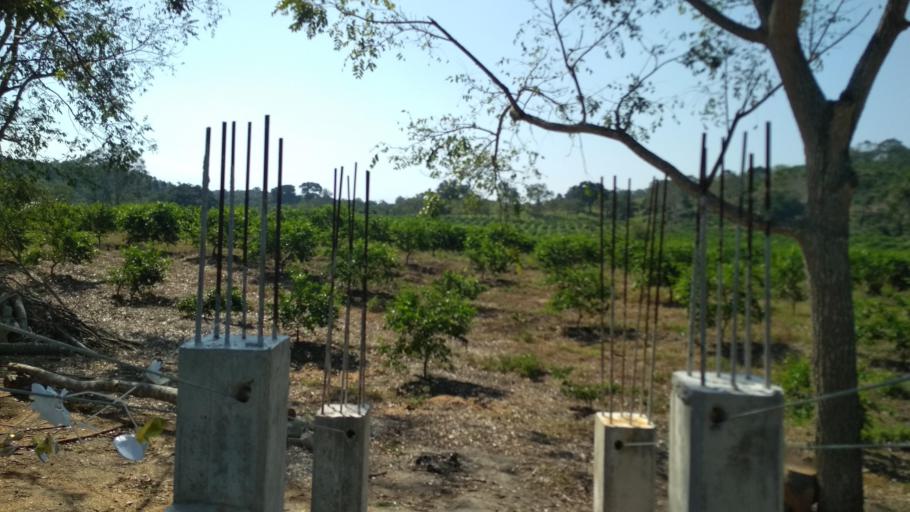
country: MX
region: Puebla
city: San Jose Acateno
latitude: 20.1563
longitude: -97.1795
